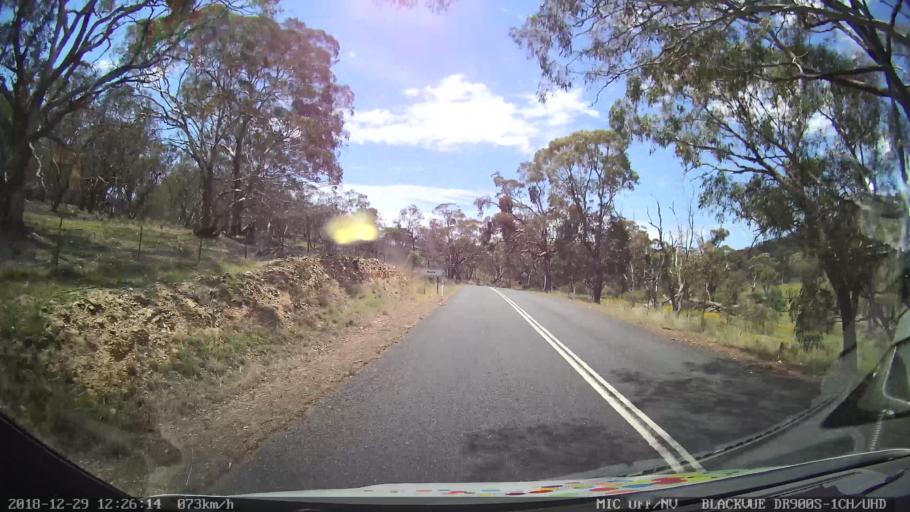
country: AU
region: New South Wales
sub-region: Queanbeyan
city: Queanbeyan
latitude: -35.4638
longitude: 149.2218
